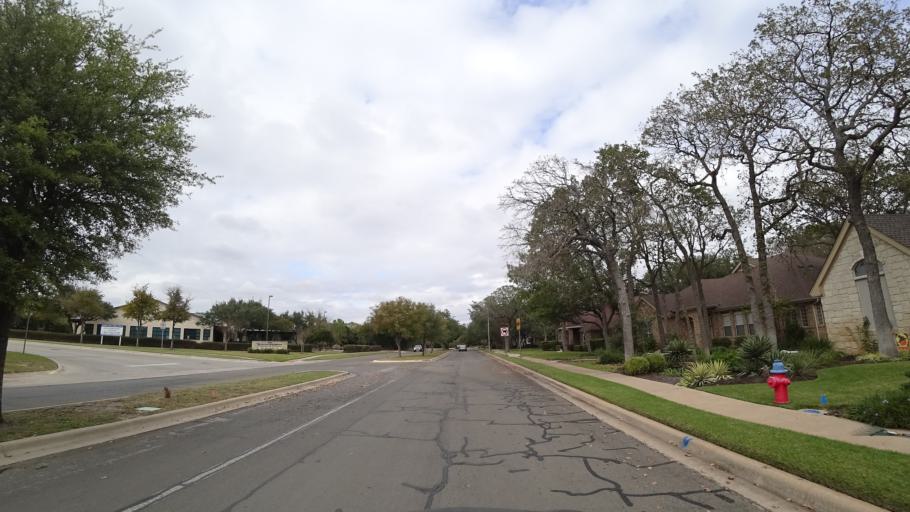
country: US
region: Texas
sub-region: Williamson County
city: Brushy Creek
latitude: 30.5126
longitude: -97.7104
